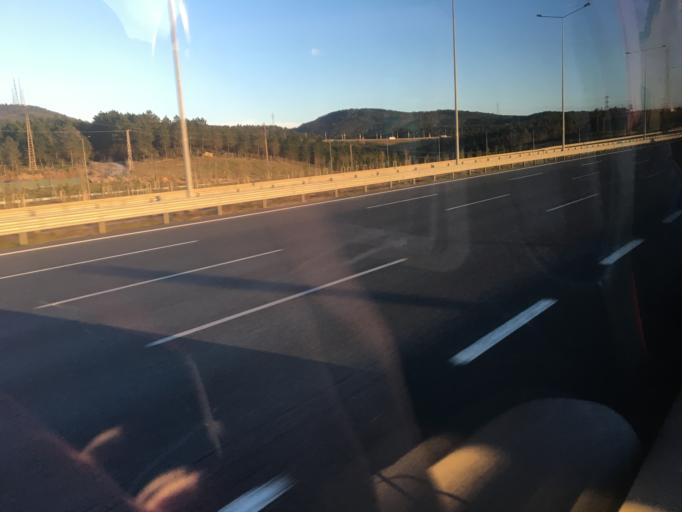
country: TR
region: Istanbul
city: Sancaktepe
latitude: 41.0551
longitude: 29.2761
